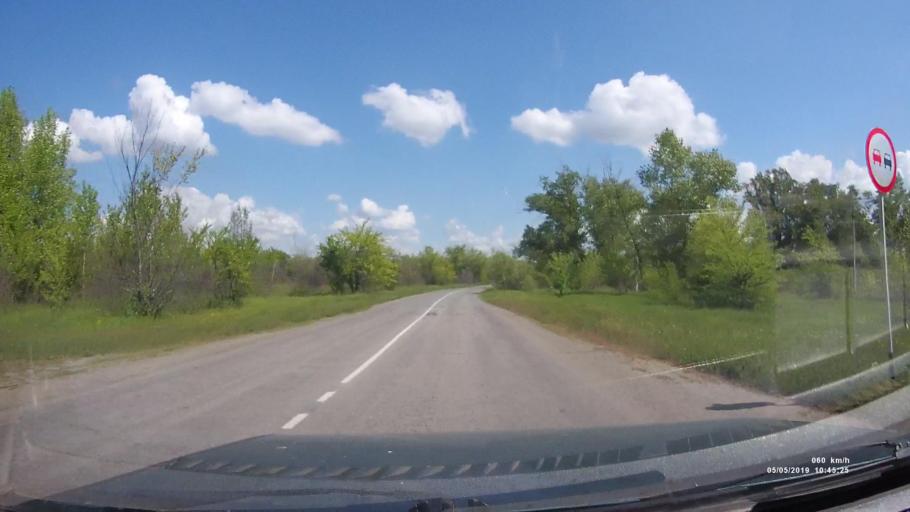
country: RU
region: Rostov
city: Ust'-Donetskiy
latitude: 47.6271
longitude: 40.8376
